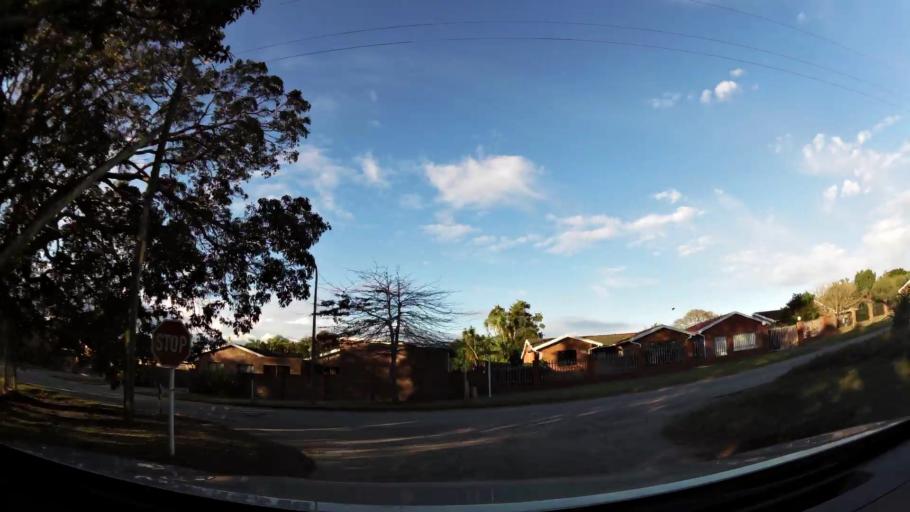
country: ZA
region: Eastern Cape
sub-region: Nelson Mandela Bay Metropolitan Municipality
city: Port Elizabeth
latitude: -33.9752
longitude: 25.4889
